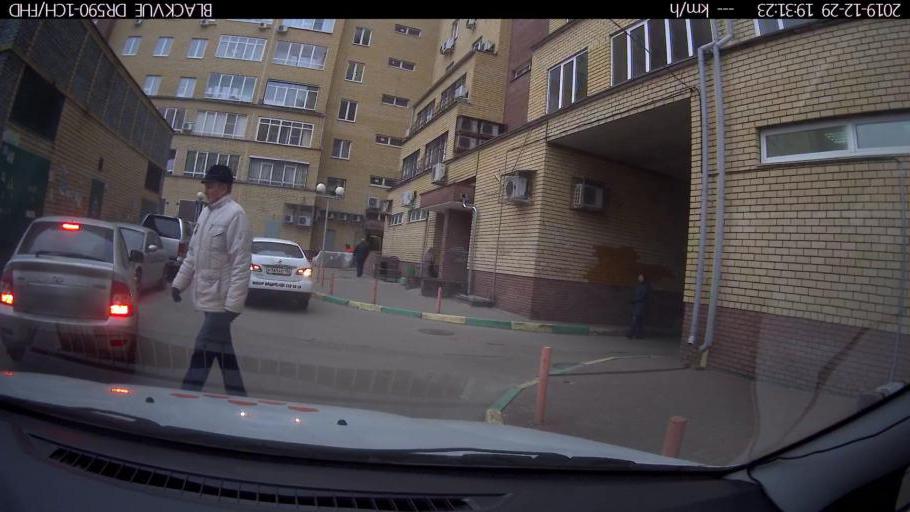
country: RU
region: Nizjnij Novgorod
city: Neklyudovo
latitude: 56.3538
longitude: 43.8671
